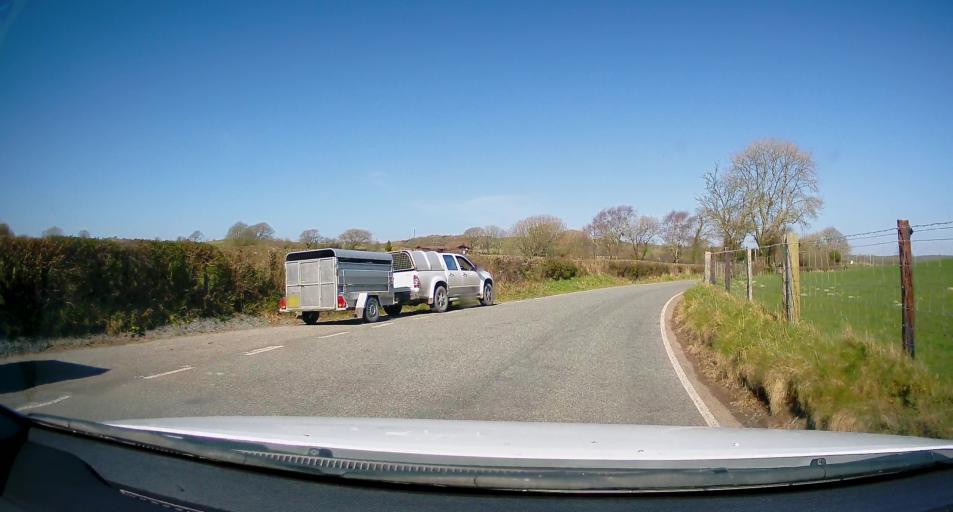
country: GB
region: Wales
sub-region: County of Ceredigion
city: Lledrod
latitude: 52.3118
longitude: -4.0620
